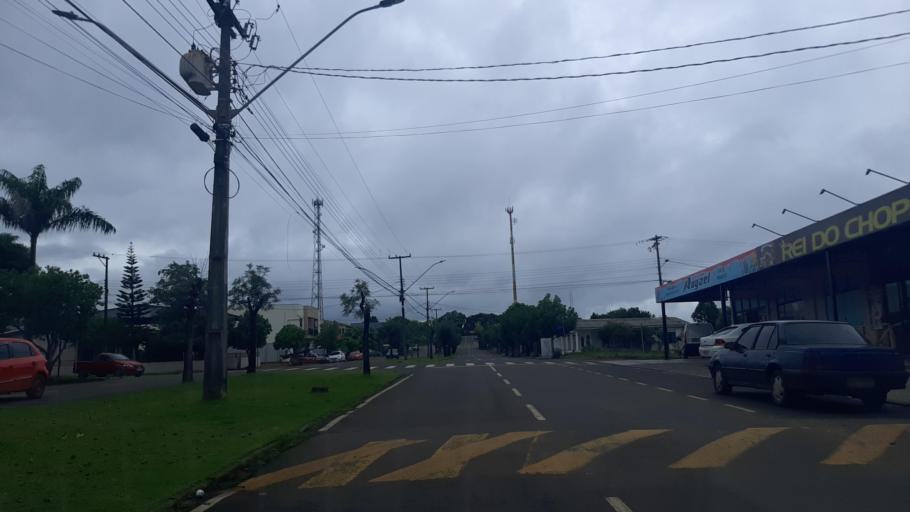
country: BR
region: Parana
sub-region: Ampere
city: Ampere
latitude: -25.9238
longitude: -53.4716
